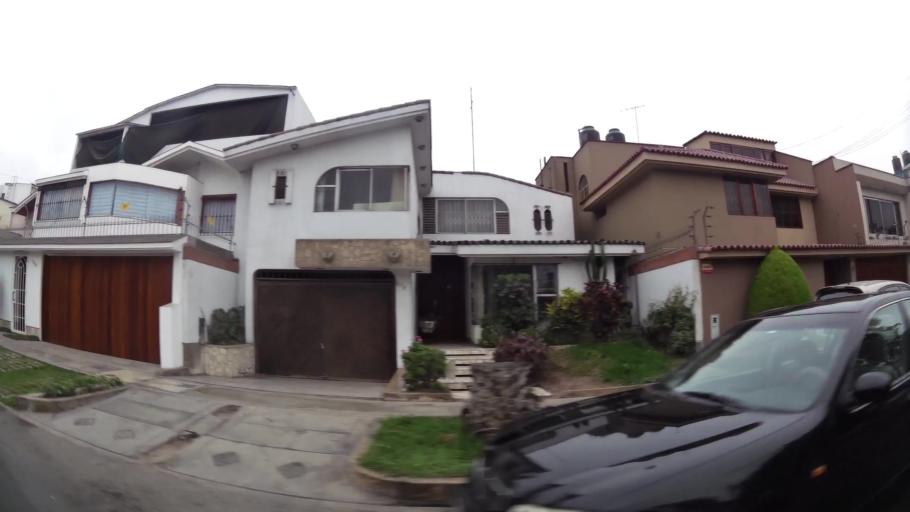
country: PE
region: Lima
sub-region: Lima
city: La Molina
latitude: -12.0714
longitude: -76.9598
